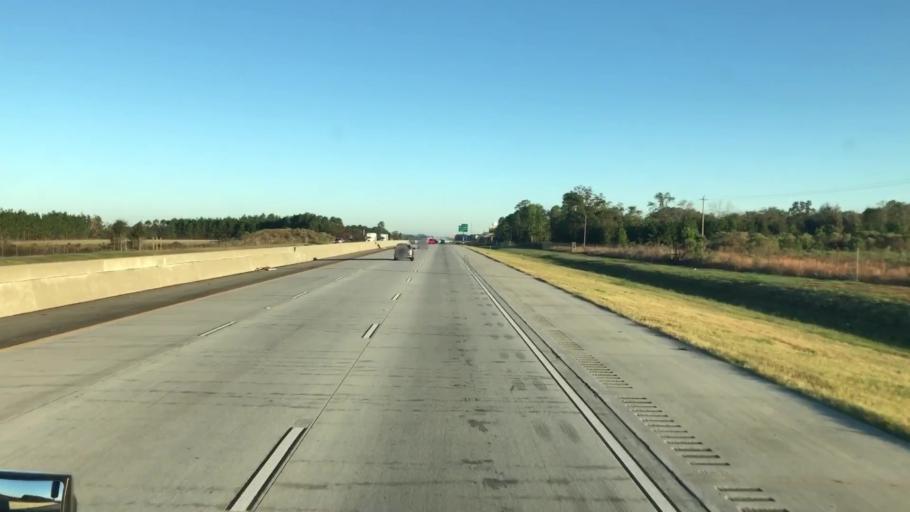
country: US
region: Georgia
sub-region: Tift County
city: Unionville
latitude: 31.3425
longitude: -83.4859
